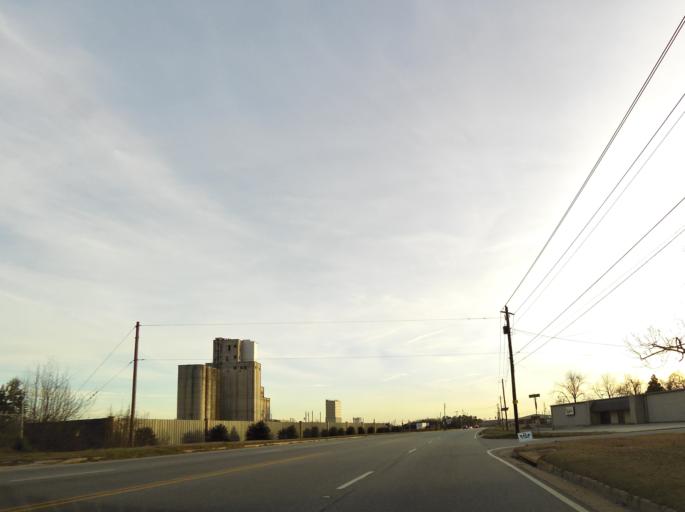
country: US
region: Georgia
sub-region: Bibb County
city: Macon
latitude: 32.7844
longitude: -83.6533
